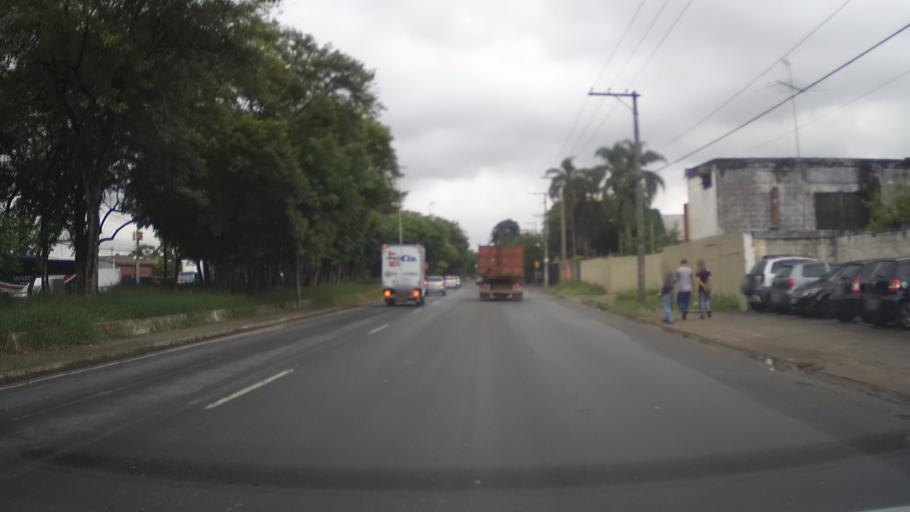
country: BR
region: Sao Paulo
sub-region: Guarulhos
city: Guarulhos
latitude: -23.4752
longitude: -46.4674
